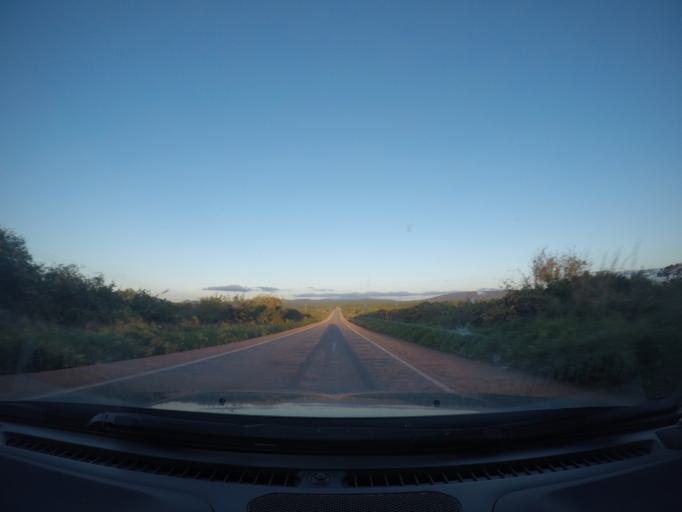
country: BR
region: Bahia
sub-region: Seabra
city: Seabra
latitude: -12.4012
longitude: -41.9456
